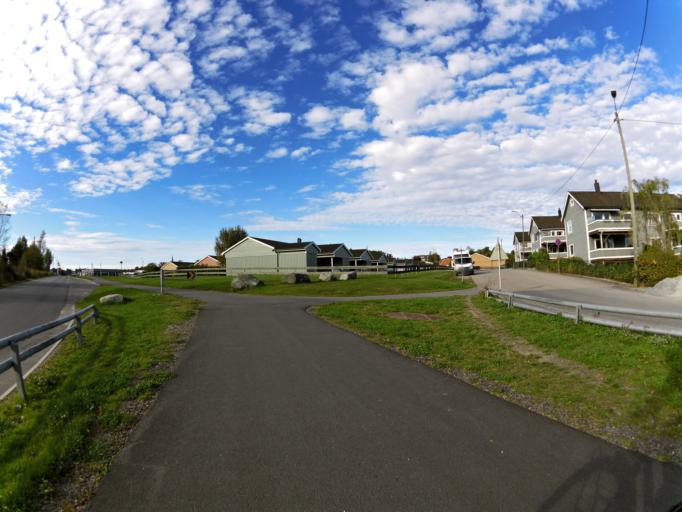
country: NO
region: Ostfold
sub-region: Sarpsborg
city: Sarpsborg
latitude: 59.2868
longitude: 11.0933
